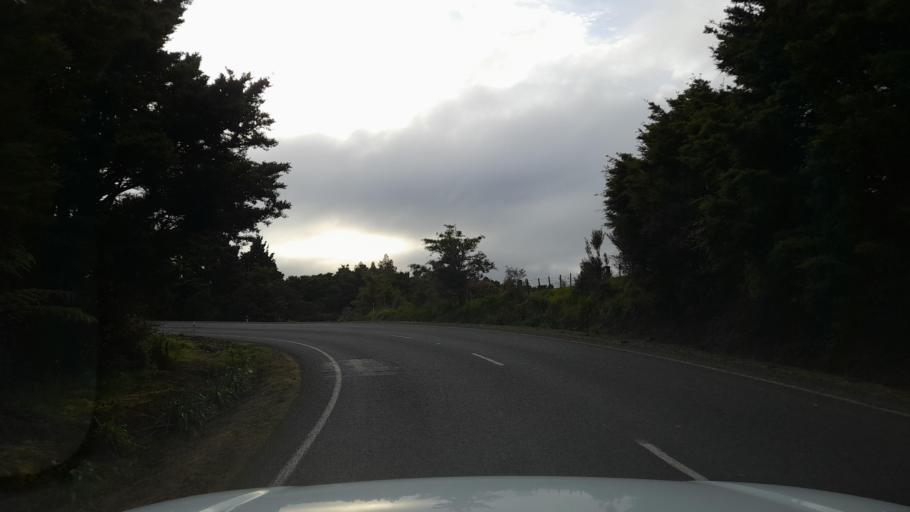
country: NZ
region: Northland
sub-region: Far North District
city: Waimate North
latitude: -35.5131
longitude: 173.8365
